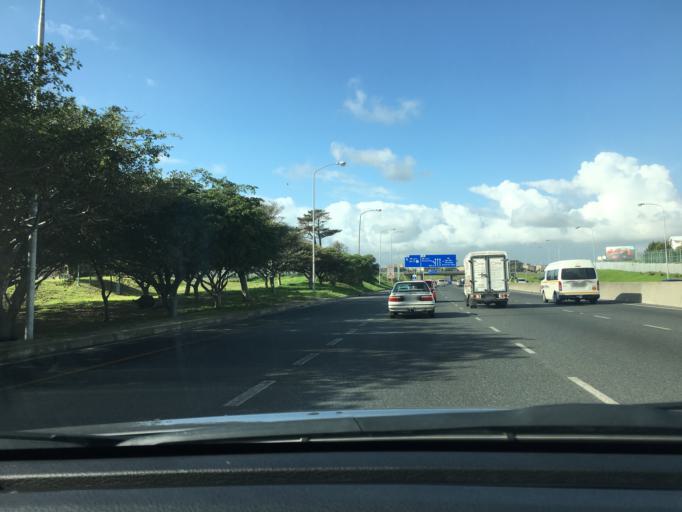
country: ZA
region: Western Cape
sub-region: City of Cape Town
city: Rosebank
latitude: -33.9438
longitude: 18.4791
